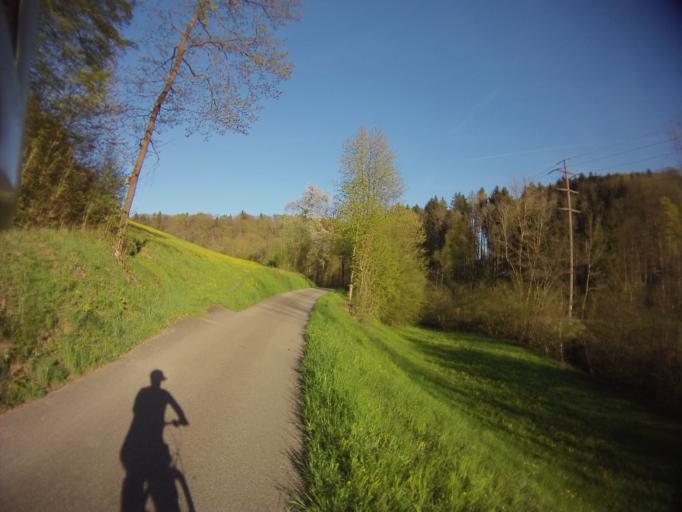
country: CH
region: Zurich
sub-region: Bezirk Dietikon
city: Birmensdorf
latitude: 47.3450
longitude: 8.4494
